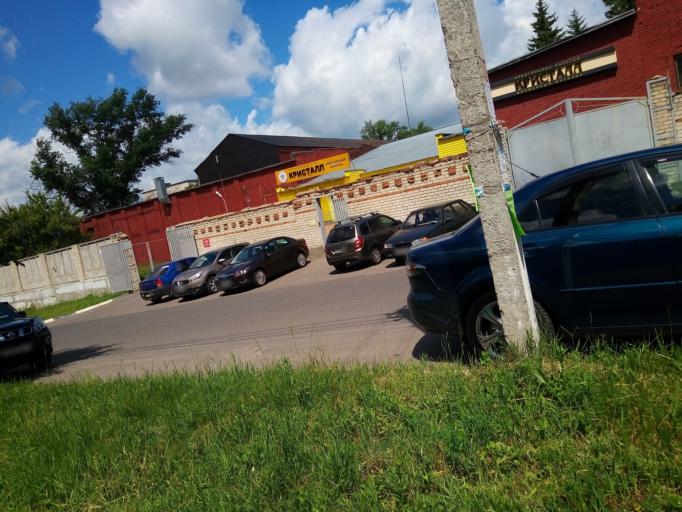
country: RU
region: Kursk
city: Kursk
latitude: 51.7442
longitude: 36.1824
